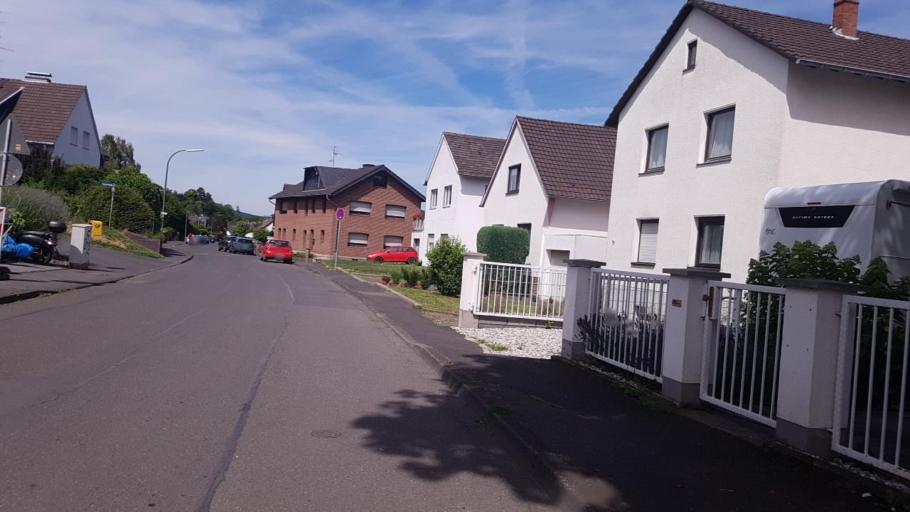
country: DE
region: North Rhine-Westphalia
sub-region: Regierungsbezirk Koln
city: Konigswinter
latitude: 50.6468
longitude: 7.1790
